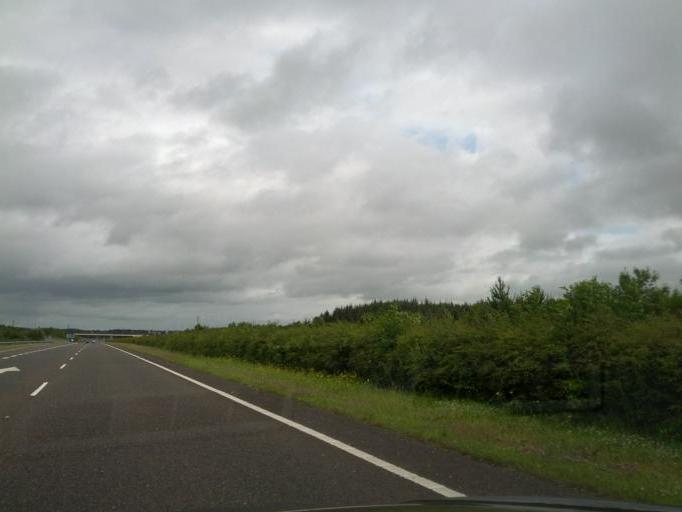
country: IE
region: Munster
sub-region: An Clar
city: Newmarket on Fergus
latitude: 52.7833
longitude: -8.9219
